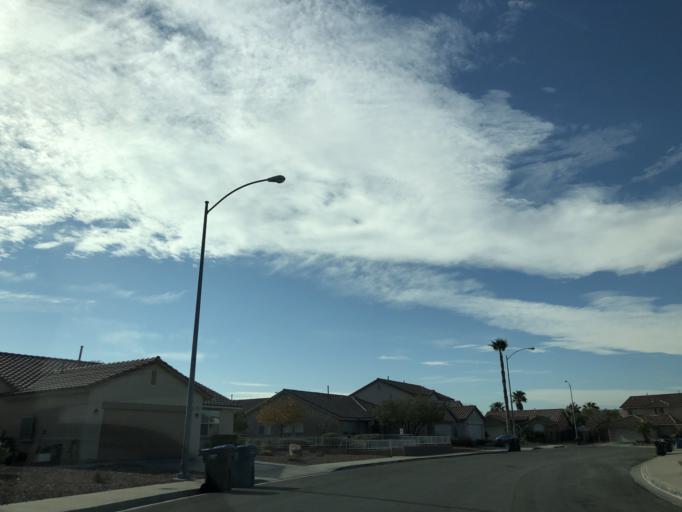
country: US
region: Nevada
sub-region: Clark County
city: Henderson
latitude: 36.0206
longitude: -115.0426
